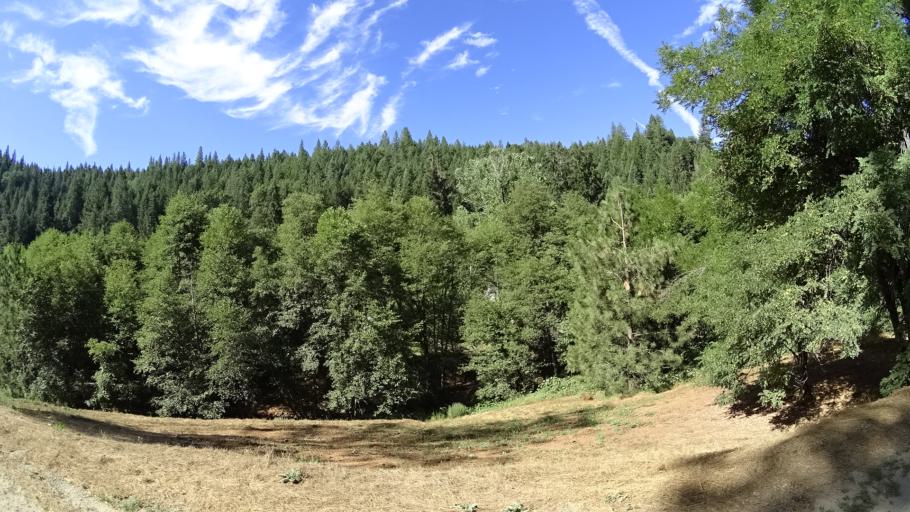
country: US
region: California
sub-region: Calaveras County
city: Arnold
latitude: 38.3680
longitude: -120.4407
